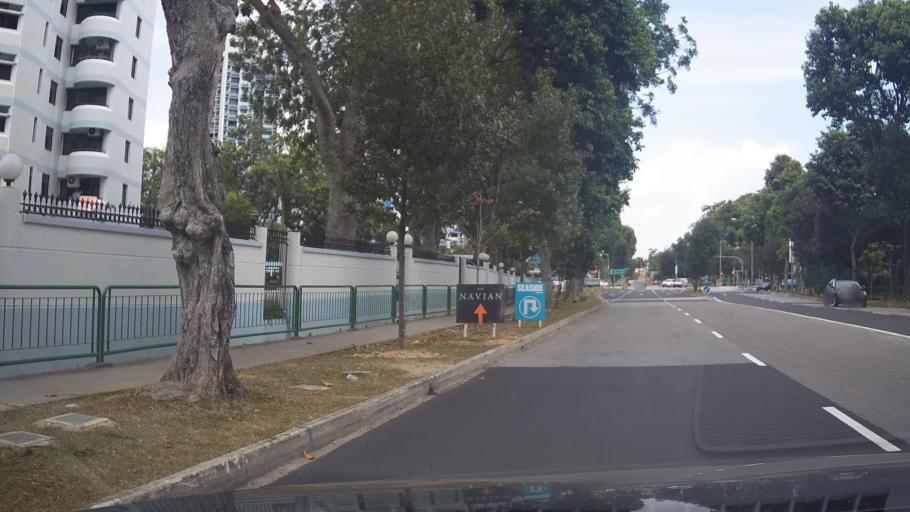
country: SG
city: Singapore
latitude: 1.3074
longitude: 103.9261
